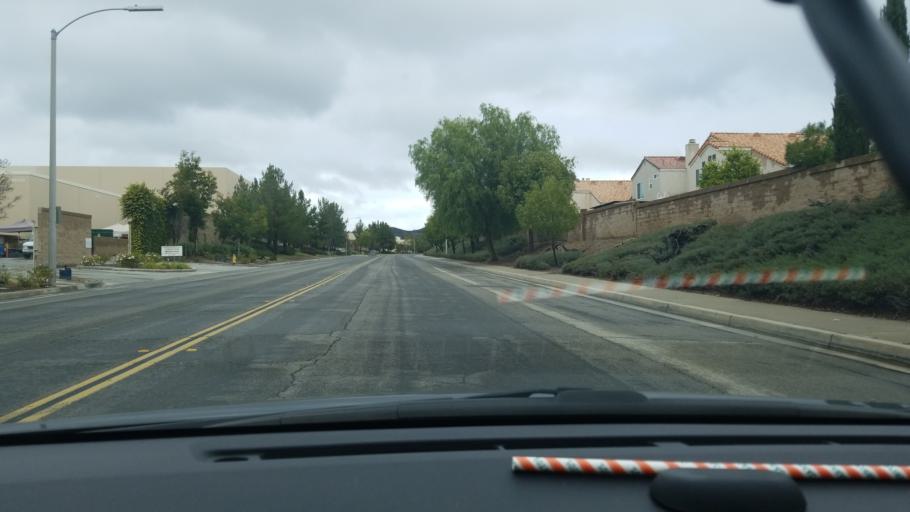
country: US
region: California
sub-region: Riverside County
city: Murrieta Hot Springs
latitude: 33.5688
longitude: -117.1791
